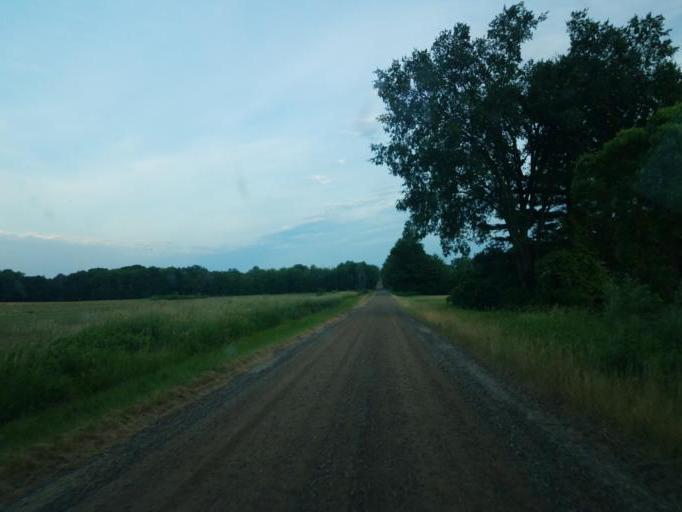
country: US
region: Michigan
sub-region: Eaton County
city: Charlotte
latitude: 42.5972
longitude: -84.8994
